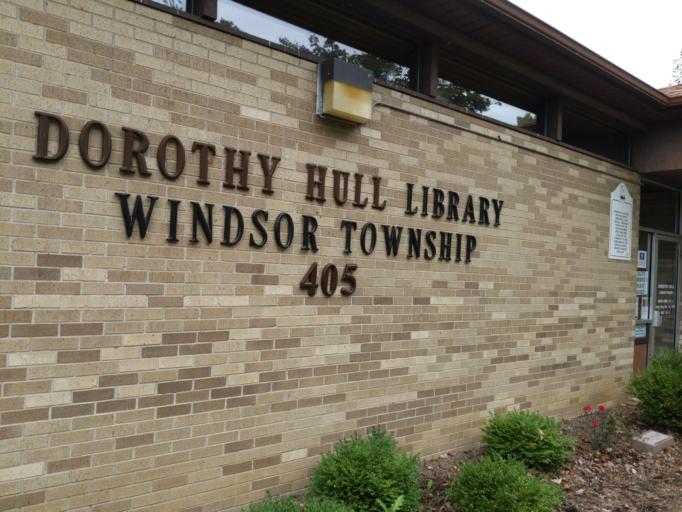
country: US
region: Michigan
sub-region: Eaton County
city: Dimondale
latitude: 42.6463
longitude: -84.6550
